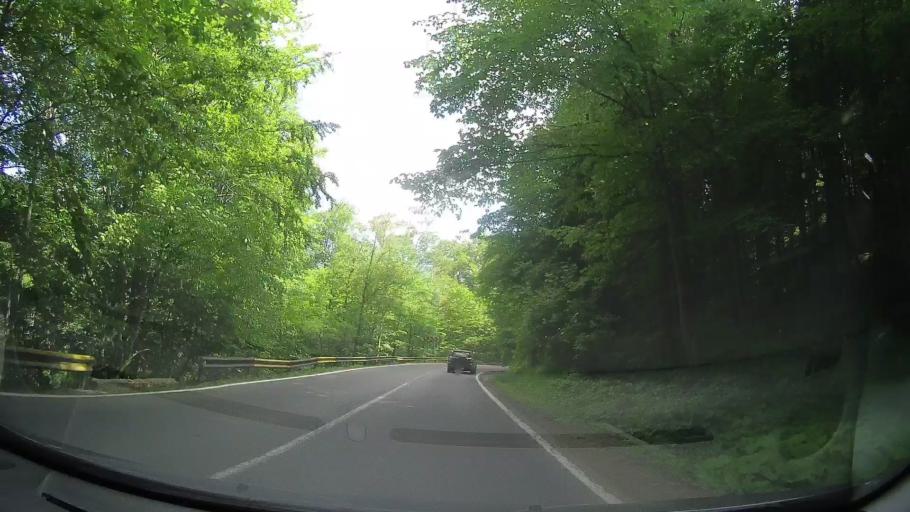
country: RO
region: Prahova
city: Maneciu
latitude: 45.3752
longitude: 25.9291
